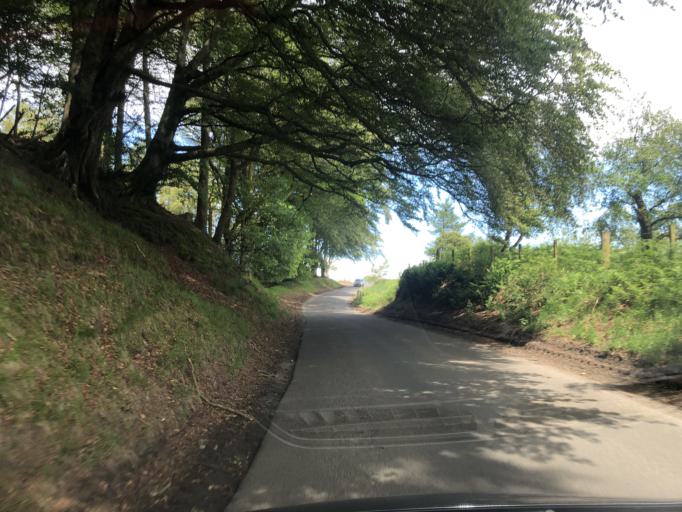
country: GB
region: Scotland
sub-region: Angus
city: Kirriemuir
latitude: 56.7655
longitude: -3.0199
